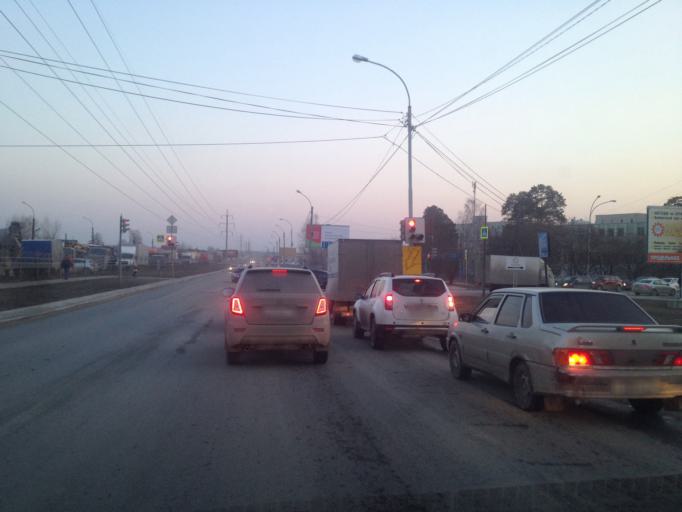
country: RU
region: Sverdlovsk
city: Sovkhoznyy
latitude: 56.7649
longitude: 60.5923
